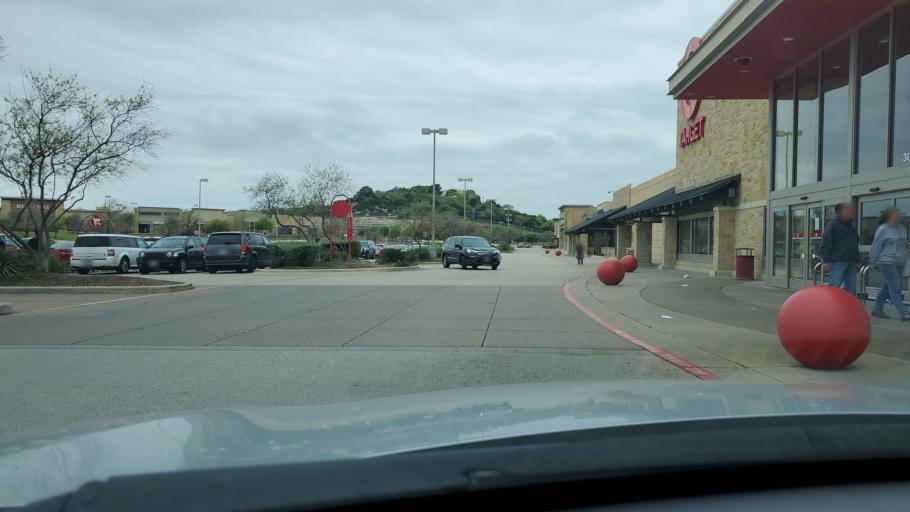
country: US
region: Texas
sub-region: Bell County
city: Harker Heights
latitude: 31.0738
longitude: -97.6622
